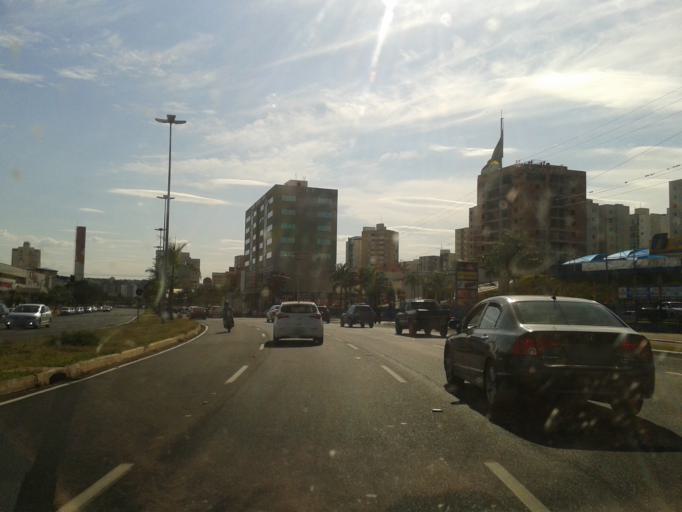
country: BR
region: Minas Gerais
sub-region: Uberlandia
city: Uberlandia
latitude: -18.9315
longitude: -48.2845
